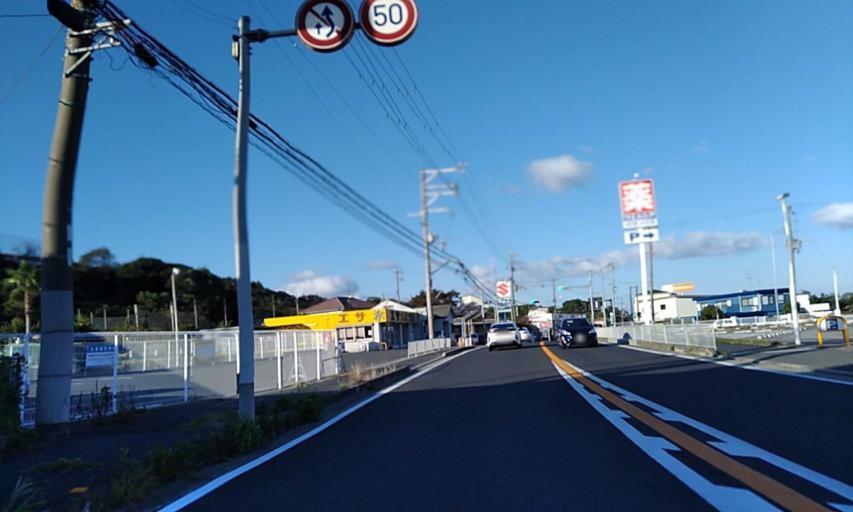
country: JP
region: Wakayama
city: Wakayama-shi
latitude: 34.3257
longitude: 135.1710
